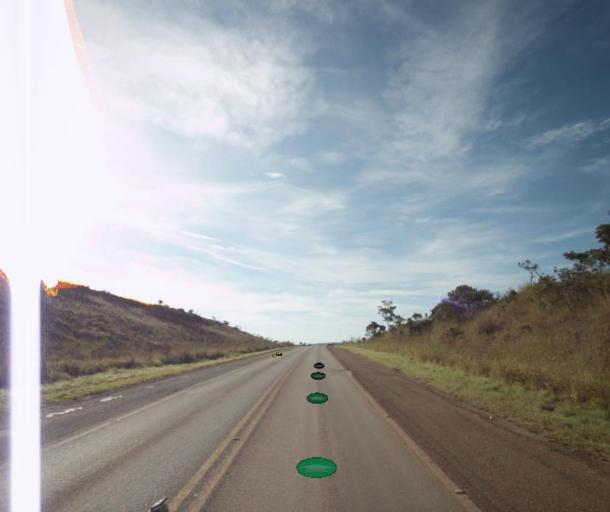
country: BR
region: Goias
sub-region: Pirenopolis
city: Pirenopolis
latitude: -15.7747
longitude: -48.5058
